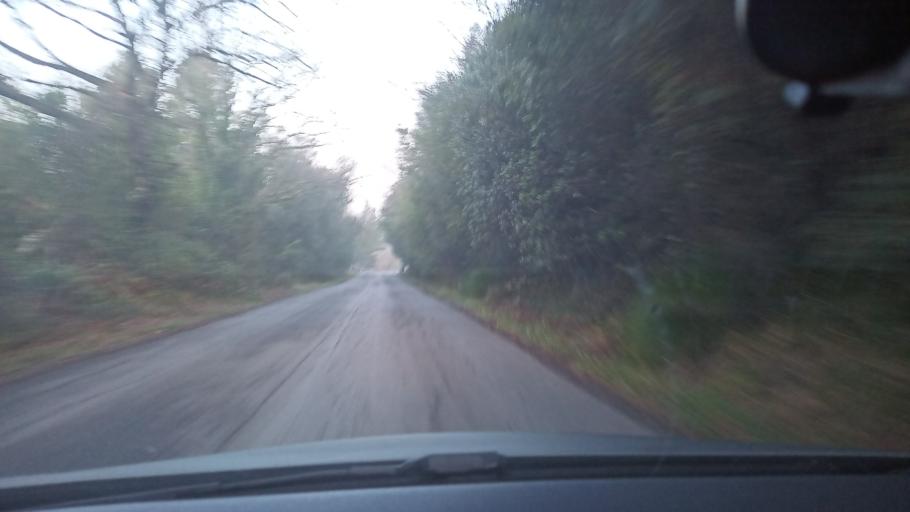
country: IT
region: Latium
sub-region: Provincia di Rieti
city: Vacone
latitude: 42.3644
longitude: 12.6629
